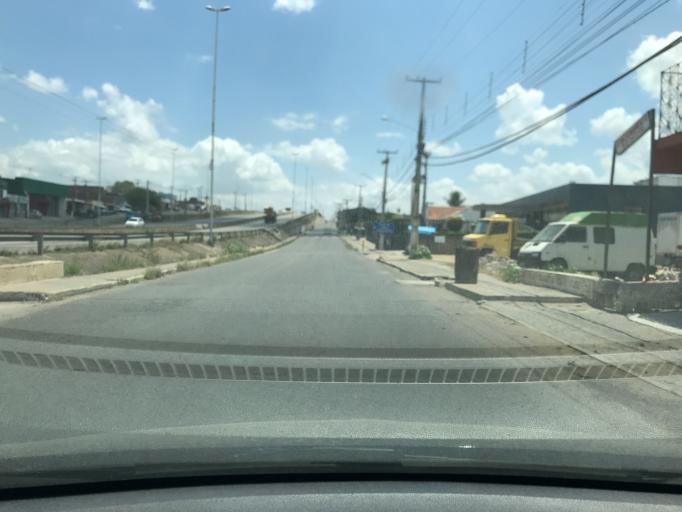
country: BR
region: Pernambuco
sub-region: Bezerros
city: Bezerros
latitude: -8.2449
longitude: -35.7555
